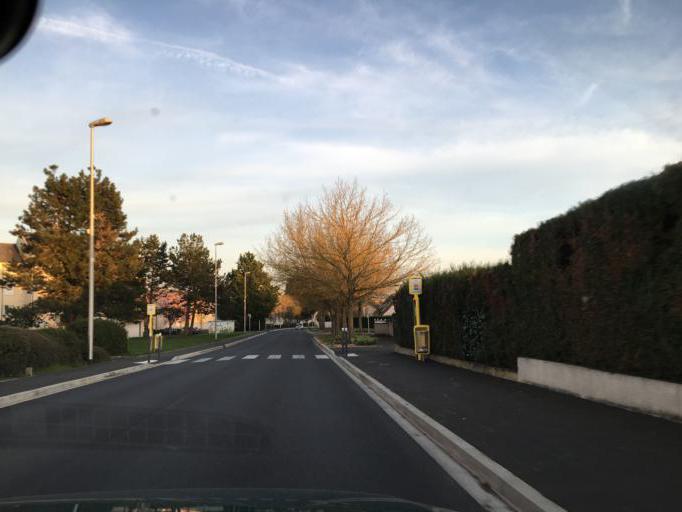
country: FR
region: Centre
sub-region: Departement du Loiret
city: Saran
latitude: 47.9388
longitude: 1.8736
